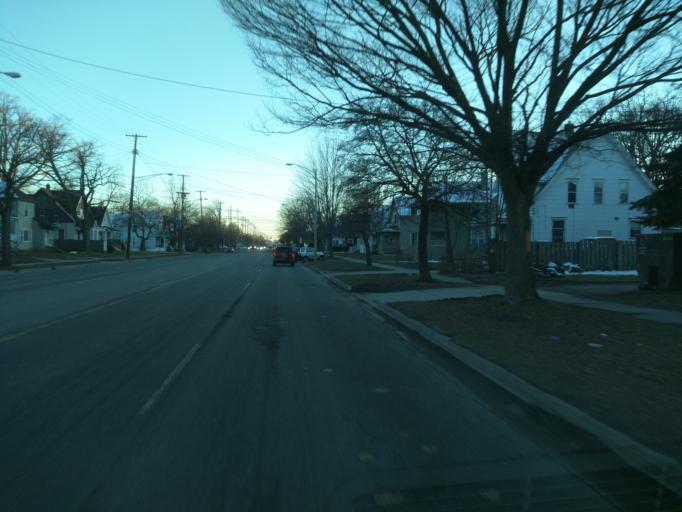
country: US
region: Michigan
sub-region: Ingham County
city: Lansing
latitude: 42.7321
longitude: -84.5380
